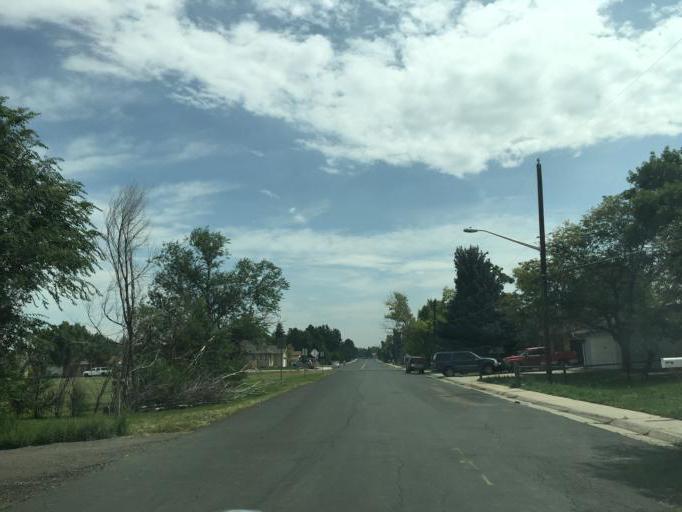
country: US
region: Colorado
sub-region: Adams County
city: Aurora
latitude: 39.7337
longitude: -104.8021
